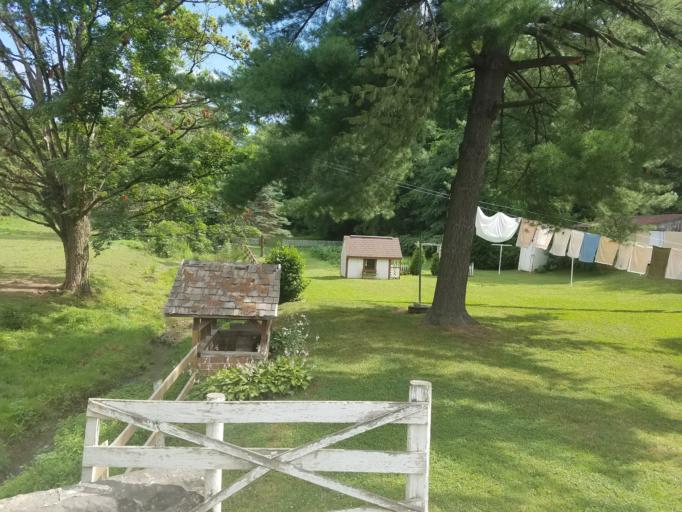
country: US
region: Ohio
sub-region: Tuscarawas County
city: Sugarcreek
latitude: 40.4253
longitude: -81.7522
